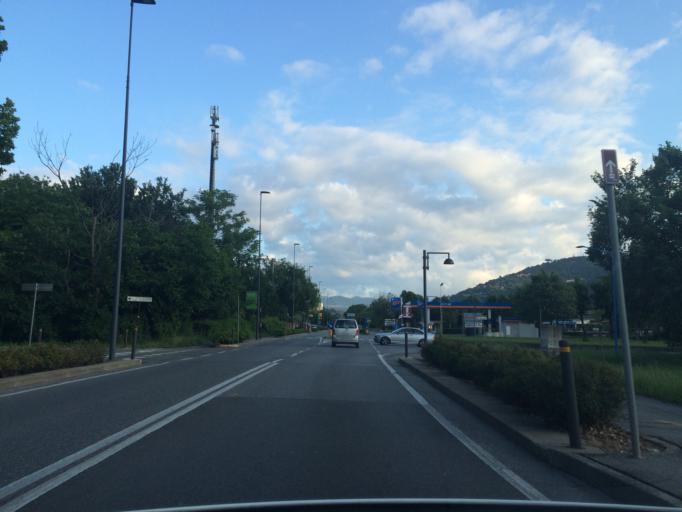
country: IT
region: Lombardy
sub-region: Provincia di Brescia
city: Brescia
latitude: 45.5200
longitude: 10.2470
